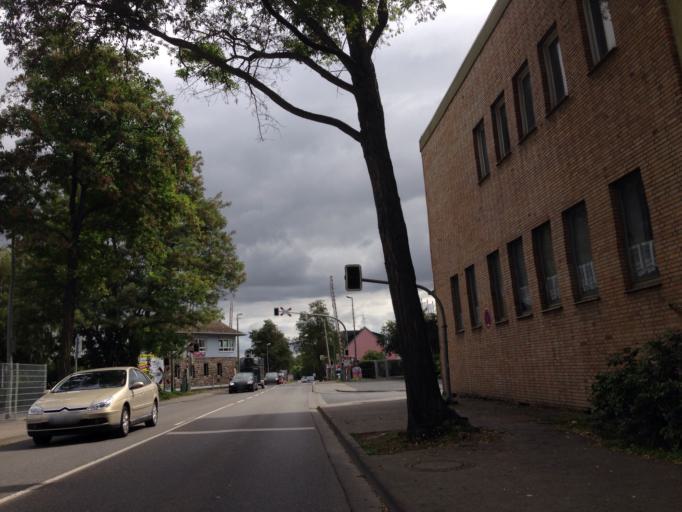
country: DE
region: Hesse
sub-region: Regierungsbezirk Giessen
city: Elz
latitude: 50.4030
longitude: 8.0426
